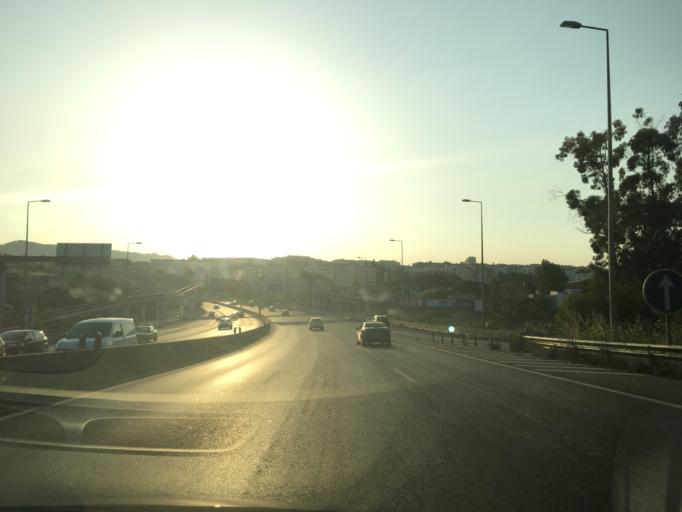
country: PT
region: Lisbon
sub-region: Sintra
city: Rio de Mouro
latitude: 38.7776
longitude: -9.3238
